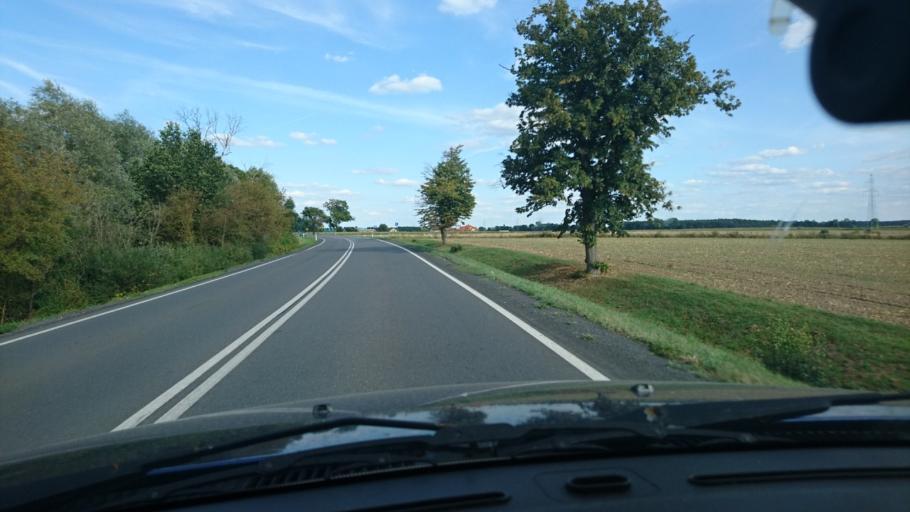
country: PL
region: Greater Poland Voivodeship
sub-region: Powiat krotoszynski
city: Zduny
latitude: 51.7179
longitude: 17.3672
